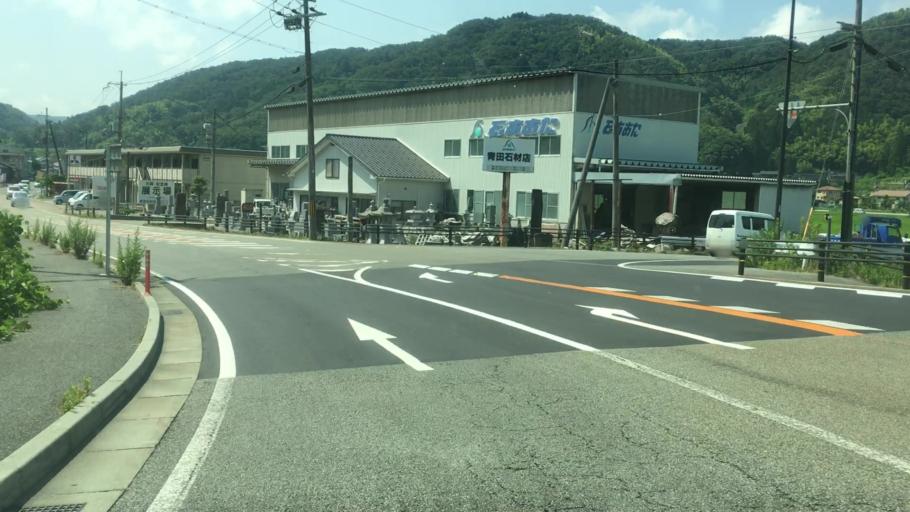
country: JP
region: Hyogo
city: Toyooka
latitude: 35.5640
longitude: 134.7952
